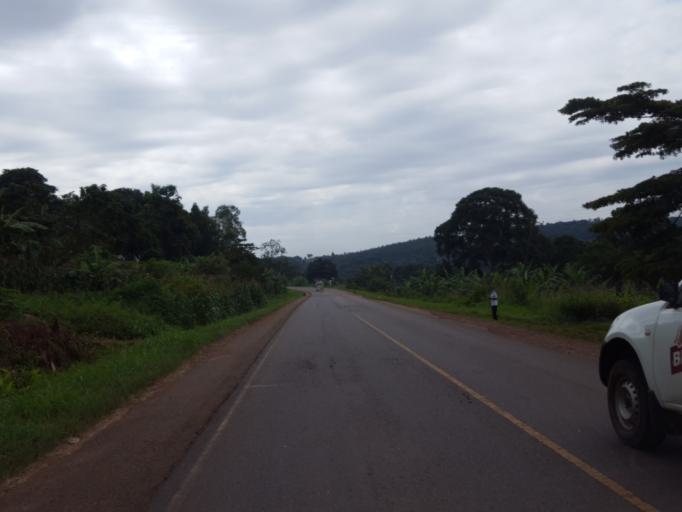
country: UG
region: Central Region
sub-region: Mityana District
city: Mityana
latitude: 0.6712
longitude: 32.0721
